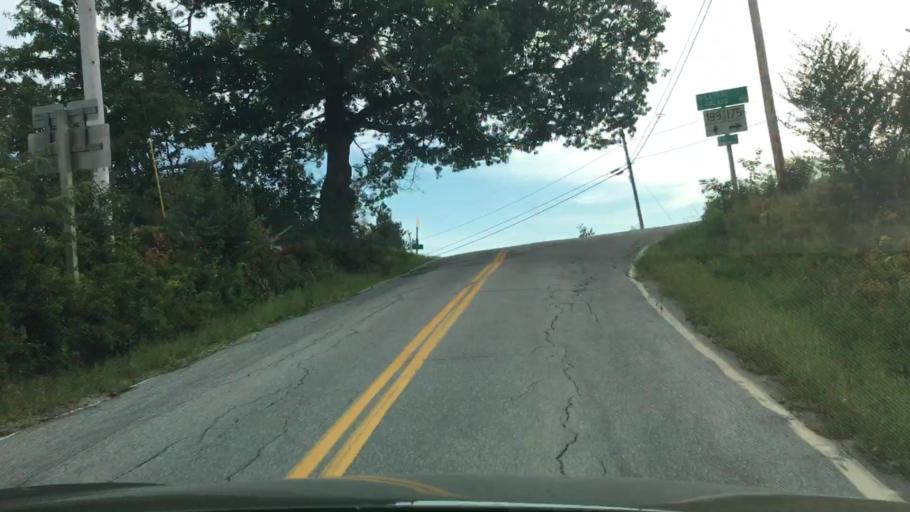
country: US
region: Maine
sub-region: Hancock County
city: Penobscot
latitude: 44.4688
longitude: -68.7393
